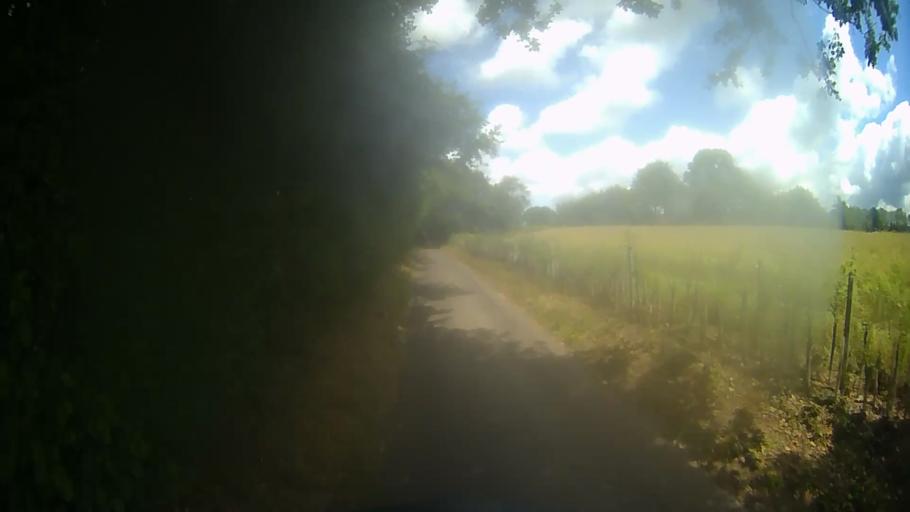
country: GB
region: England
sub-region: Hampshire
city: Andover
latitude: 51.2575
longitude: -1.4337
